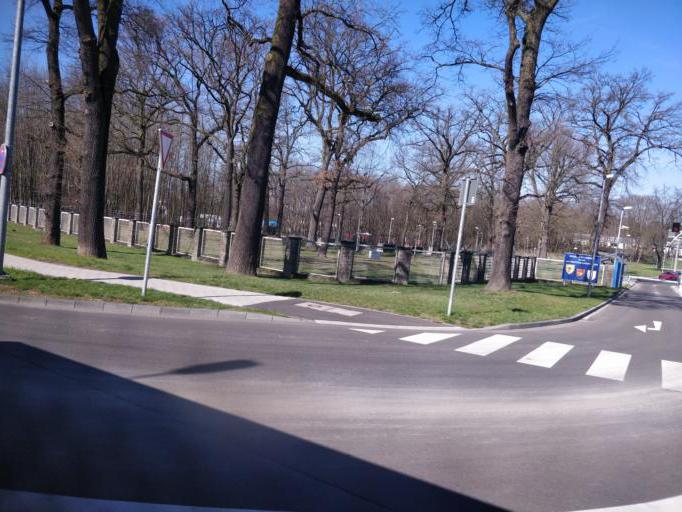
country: DE
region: North Rhine-Westphalia
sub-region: Regierungsbezirk Koln
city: Wahn-Heide
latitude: 50.8558
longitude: 7.1115
